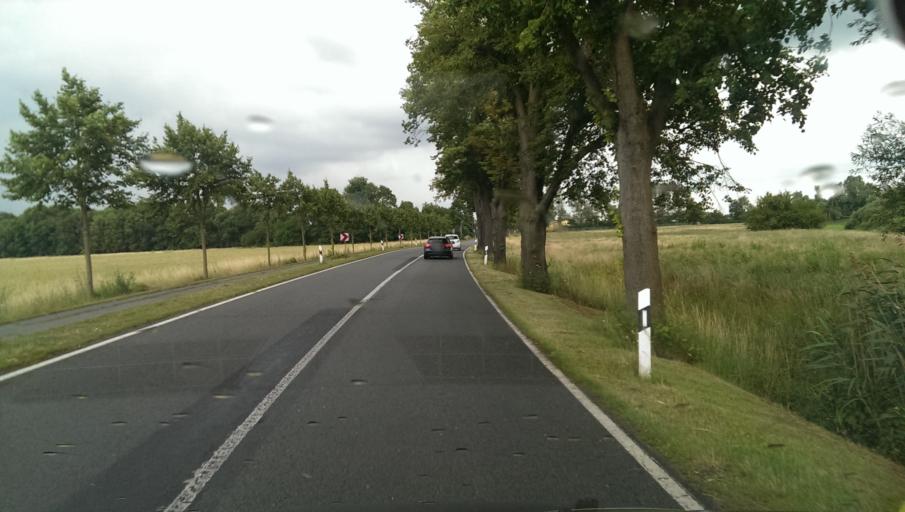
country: DE
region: Brandenburg
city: Rathenow
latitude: 52.6317
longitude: 12.3322
